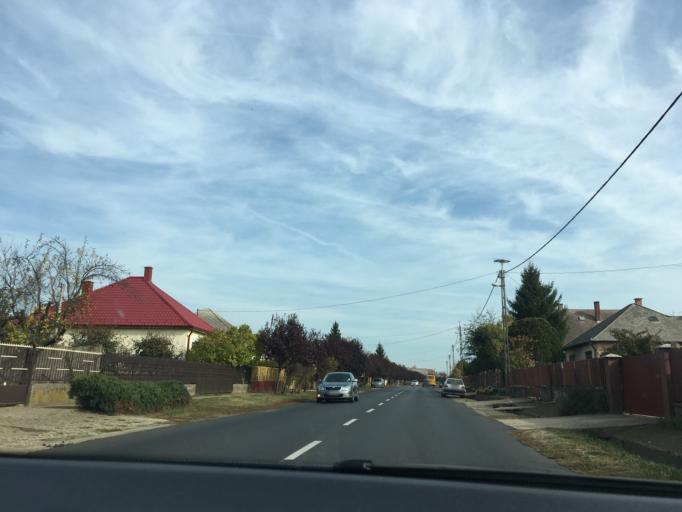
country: HU
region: Szabolcs-Szatmar-Bereg
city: Kallosemjen
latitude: 47.8599
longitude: 21.9104
